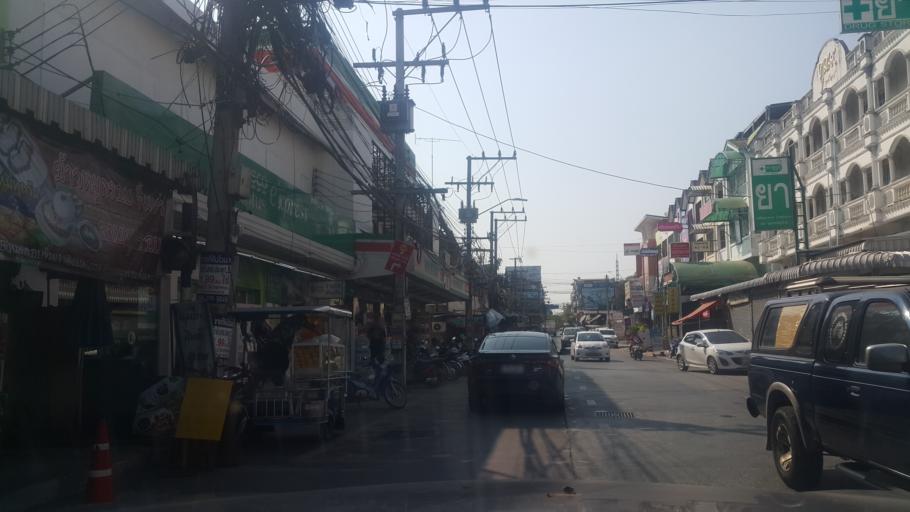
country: TH
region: Nakhon Ratchasima
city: Nakhon Ratchasima
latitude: 14.9503
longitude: 102.0446
